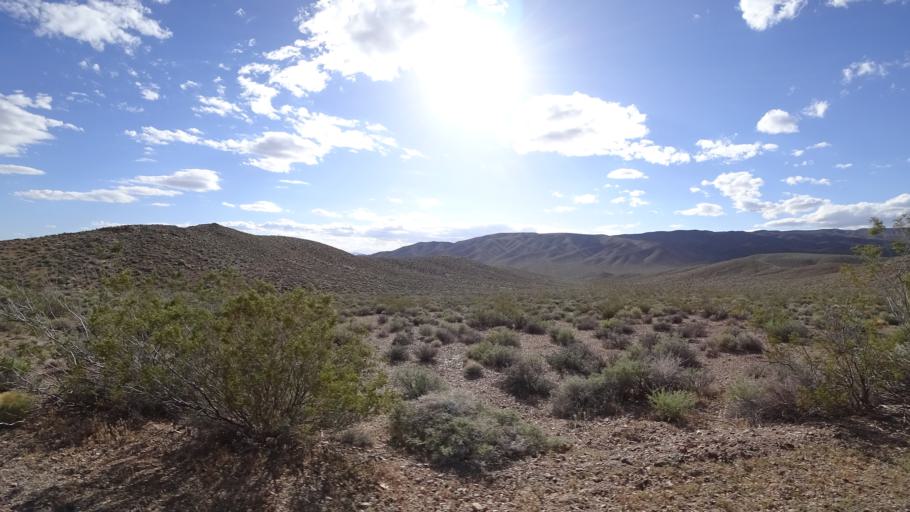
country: US
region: California
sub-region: San Bernardino County
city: Searles Valley
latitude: 36.2960
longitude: -117.1753
